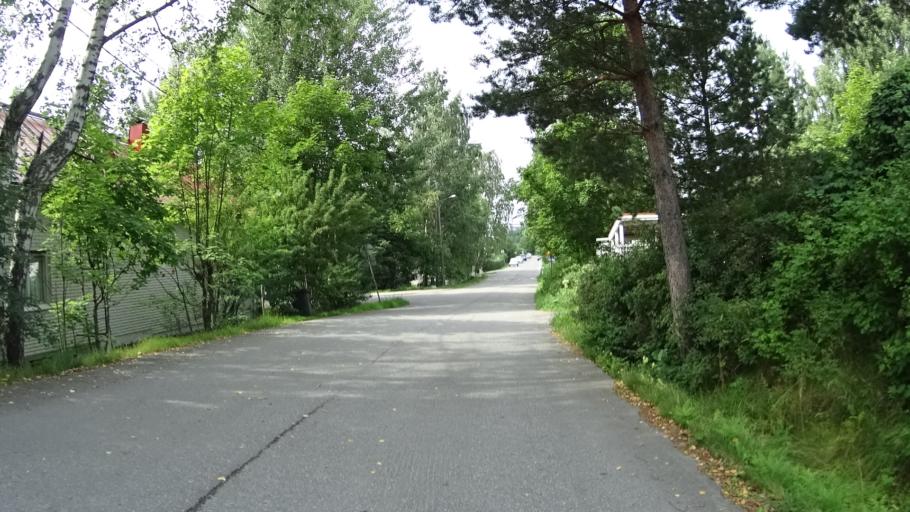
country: FI
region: Uusimaa
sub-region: Helsinki
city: Teekkarikylae
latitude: 60.2186
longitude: 24.8436
